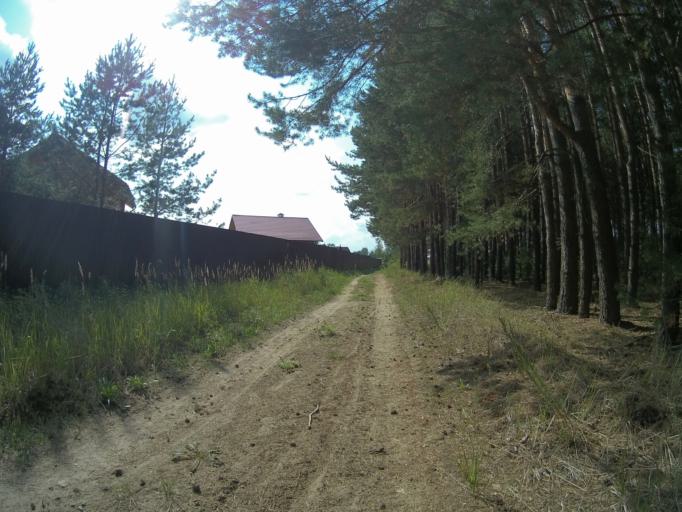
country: RU
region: Vladimir
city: Raduzhnyy
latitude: 56.0283
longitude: 40.3229
